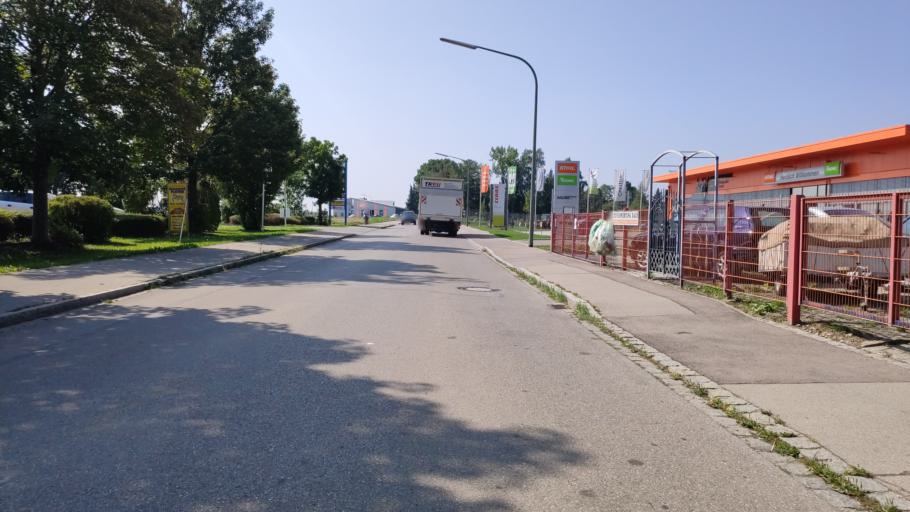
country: DE
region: Bavaria
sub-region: Swabia
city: Bobingen
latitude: 48.2660
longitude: 10.8434
